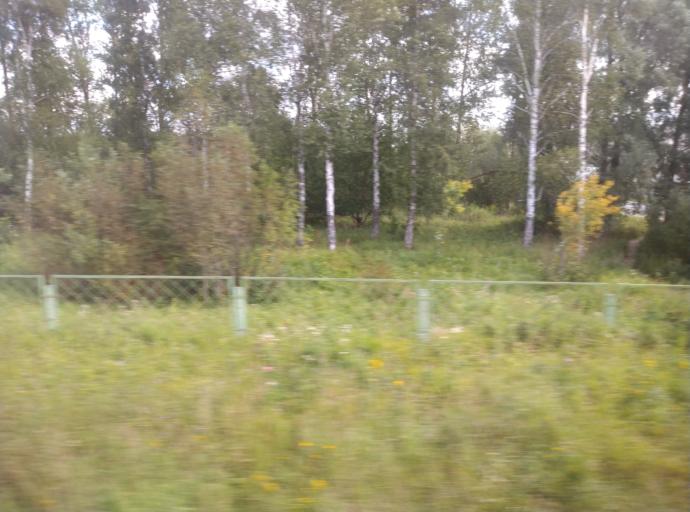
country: RU
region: St.-Petersburg
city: Kolpino
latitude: 59.7401
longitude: 30.6263
